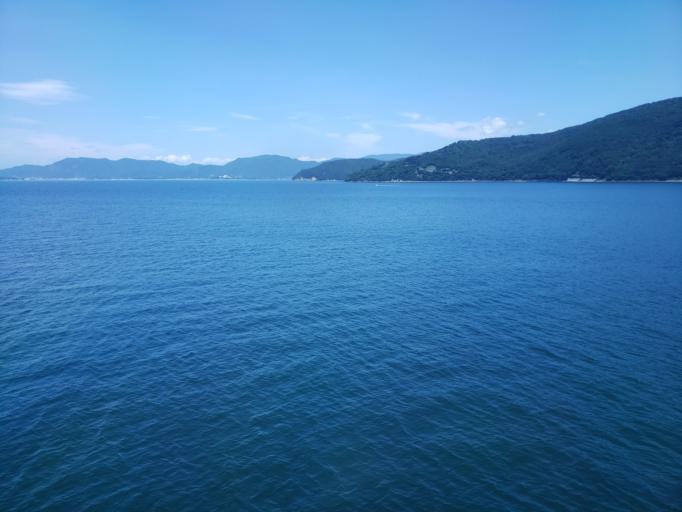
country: JP
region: Kagawa
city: Tonosho
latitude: 34.4074
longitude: 134.2210
